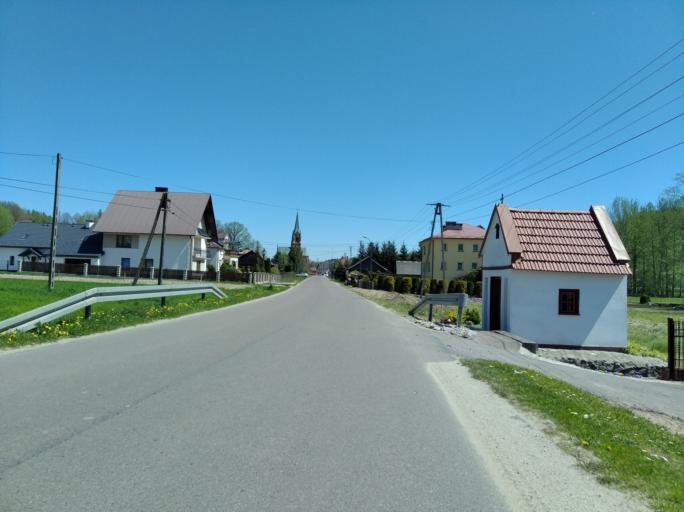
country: PL
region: Subcarpathian Voivodeship
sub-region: Powiat debicki
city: Brzostek
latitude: 49.9148
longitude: 21.4117
